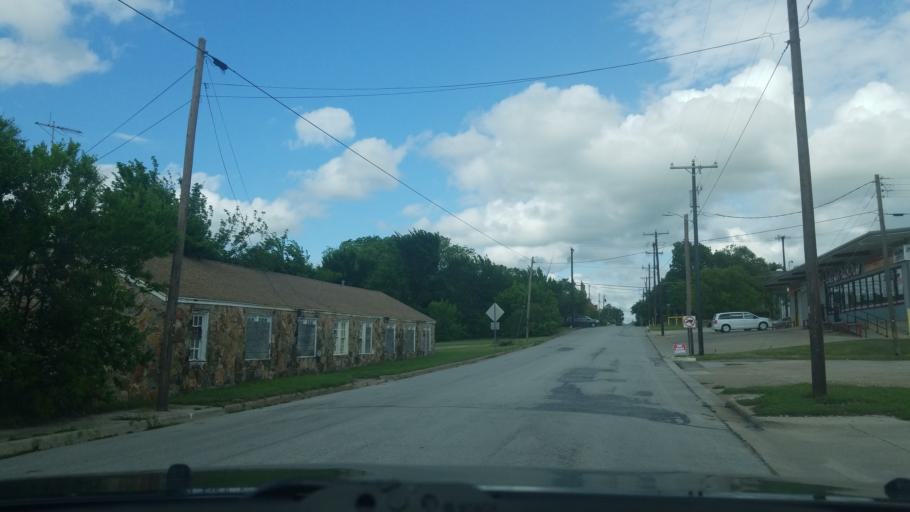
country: US
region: Texas
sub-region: Wise County
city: Decatur
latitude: 33.2342
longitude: -97.5935
